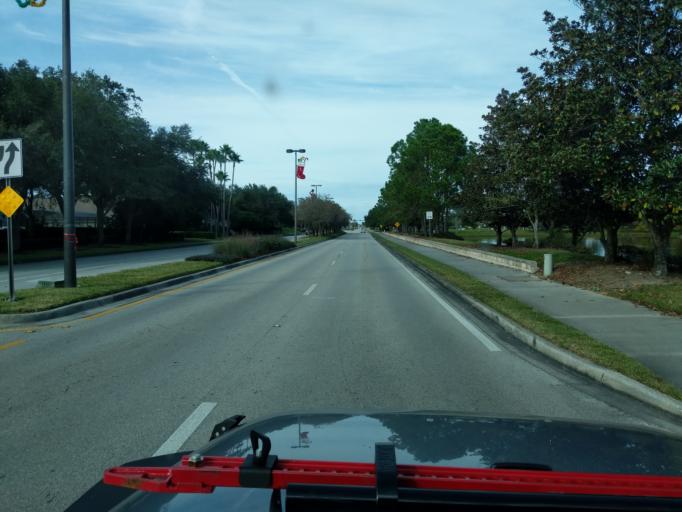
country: US
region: Florida
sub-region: Orange County
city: Gotha
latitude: 28.5354
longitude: -81.5418
